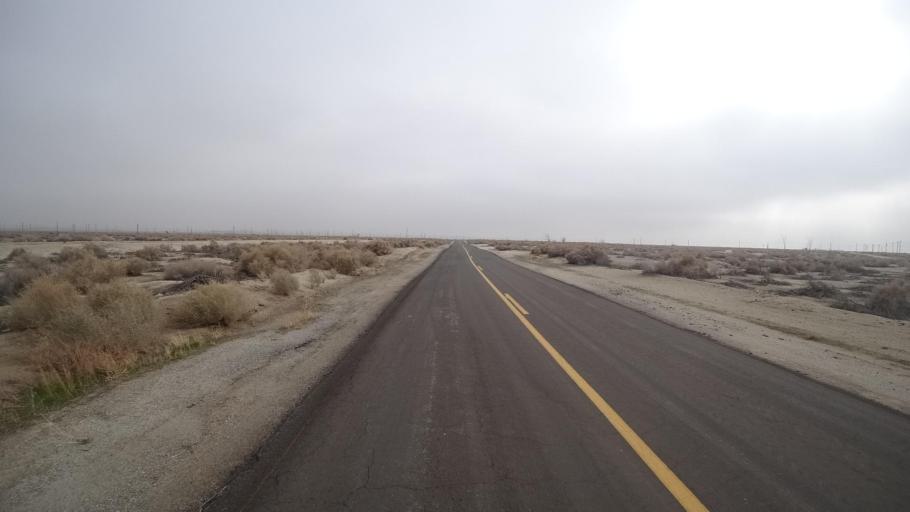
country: US
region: California
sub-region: Kern County
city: Maricopa
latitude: 35.0808
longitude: -119.3830
